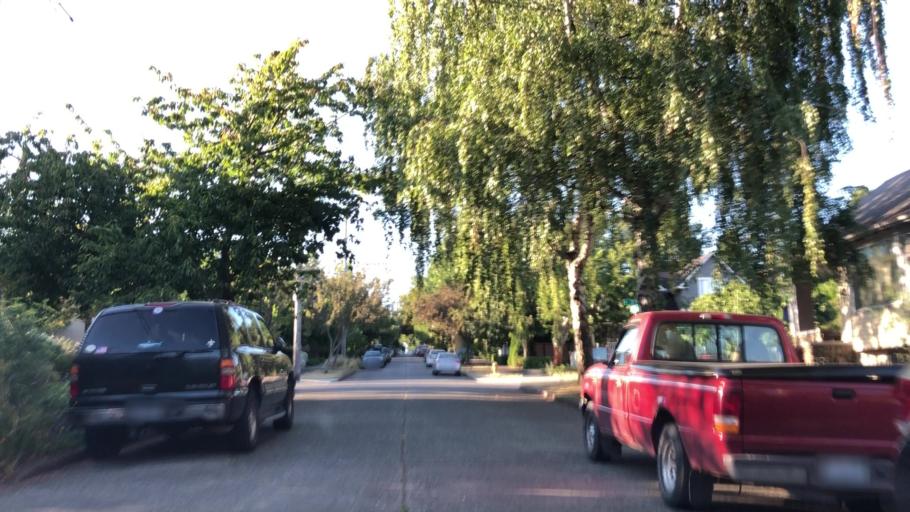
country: US
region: Washington
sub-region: King County
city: Seattle
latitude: 47.6516
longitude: -122.3351
